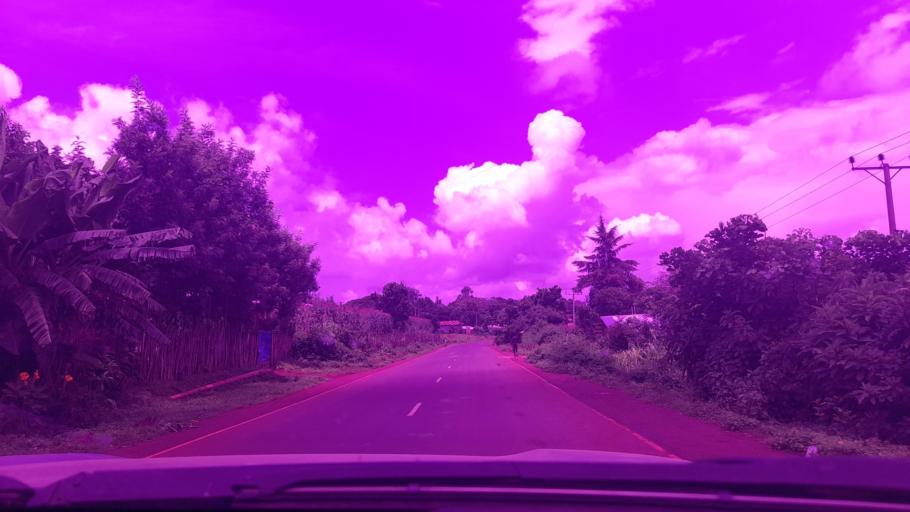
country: ET
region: Oromiya
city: Metu
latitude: 8.3368
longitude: 35.7343
